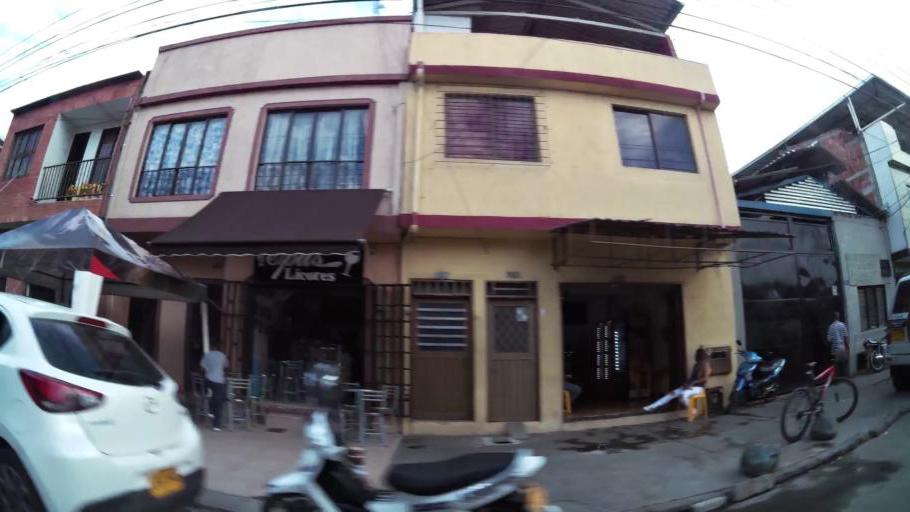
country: CO
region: Valle del Cauca
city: Cali
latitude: 3.4601
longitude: -76.5157
